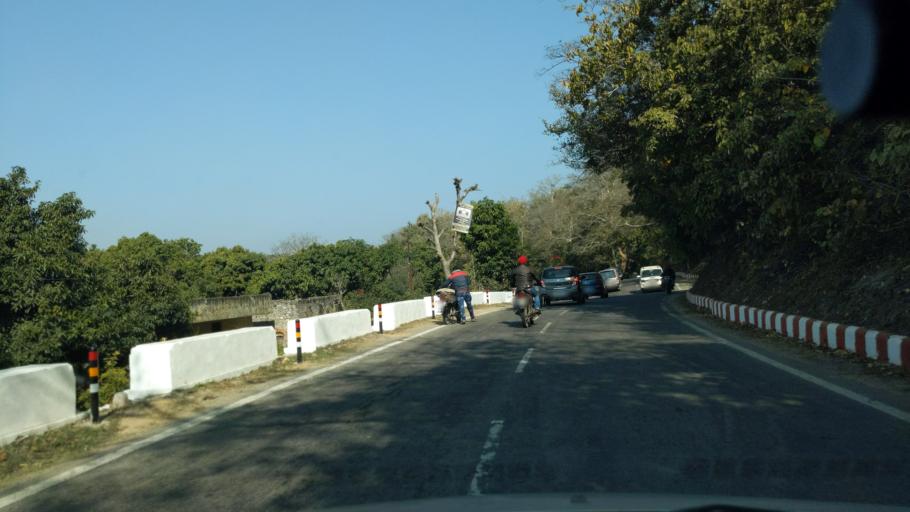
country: IN
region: Uttarakhand
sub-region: Naini Tal
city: Ramnagar
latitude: 29.3880
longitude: 79.1403
